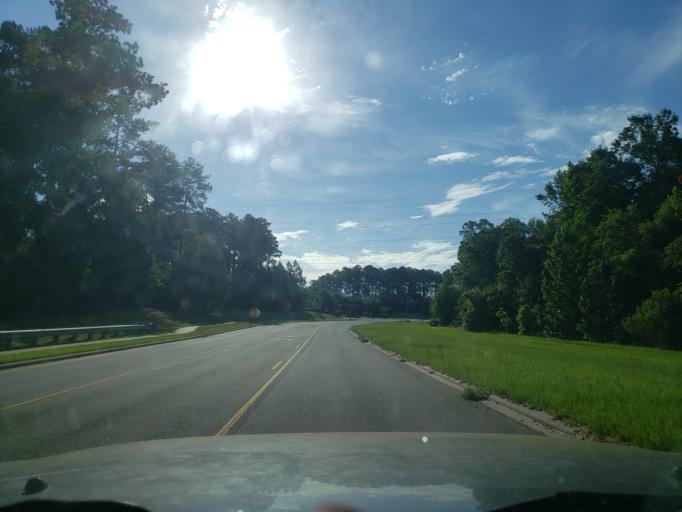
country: US
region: North Carolina
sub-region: Durham County
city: Durham
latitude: 35.9436
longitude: -78.8692
